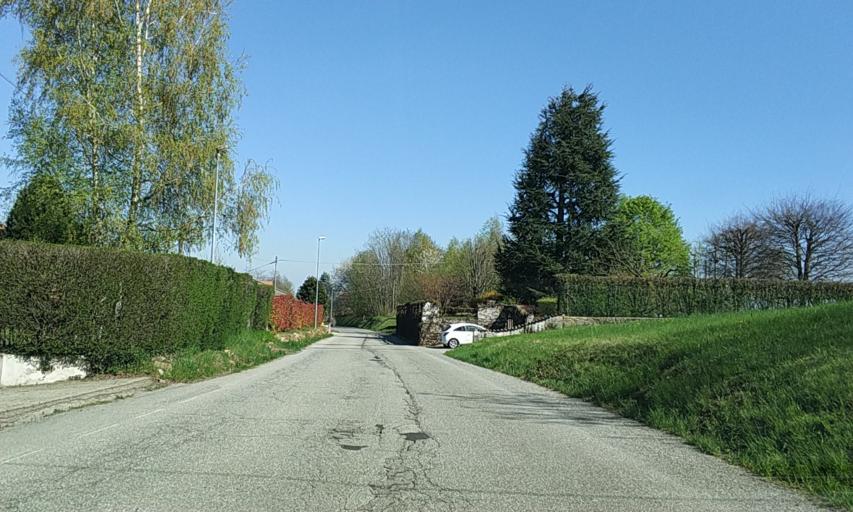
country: IT
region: Piedmont
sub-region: Provincia di Torino
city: Forno Canavese
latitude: 45.3353
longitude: 7.5960
